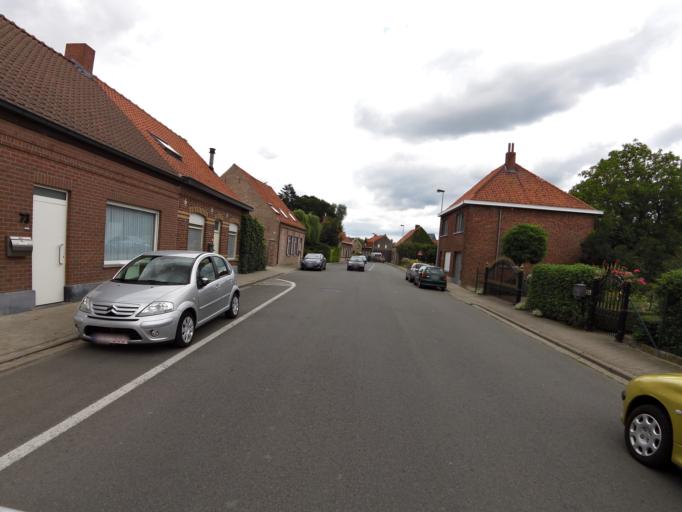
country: BE
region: Flanders
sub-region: Provincie West-Vlaanderen
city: Hooglede
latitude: 50.9815
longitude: 3.0725
